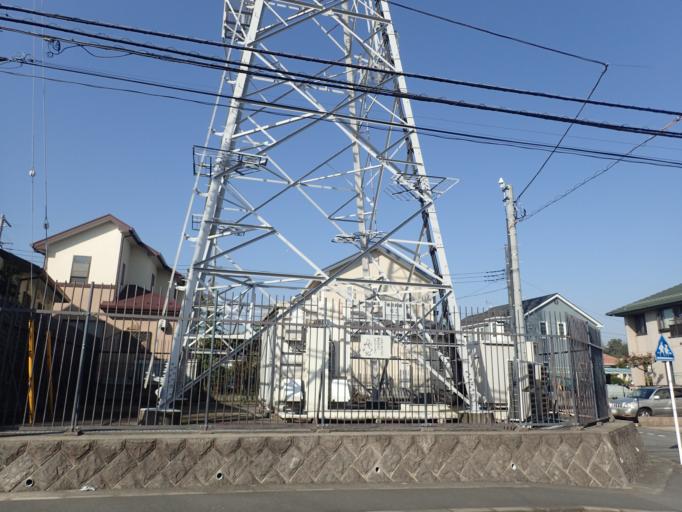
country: JP
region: Kanagawa
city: Yokosuka
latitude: 35.2959
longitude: 139.6256
